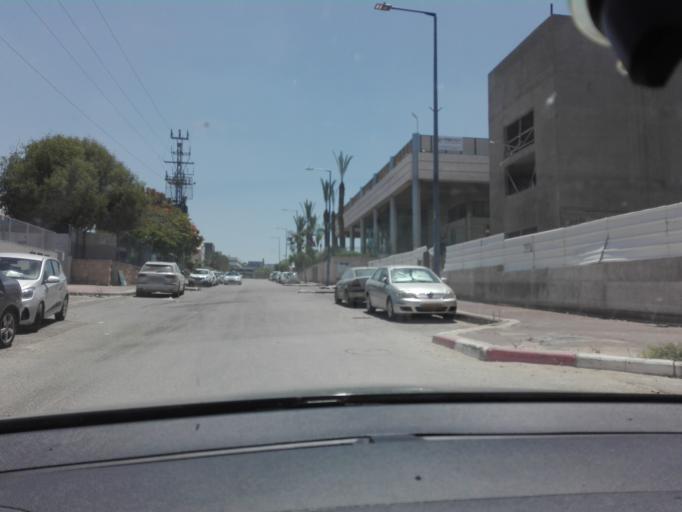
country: IL
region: Southern District
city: Qiryat Gat
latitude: 31.5940
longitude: 34.7820
